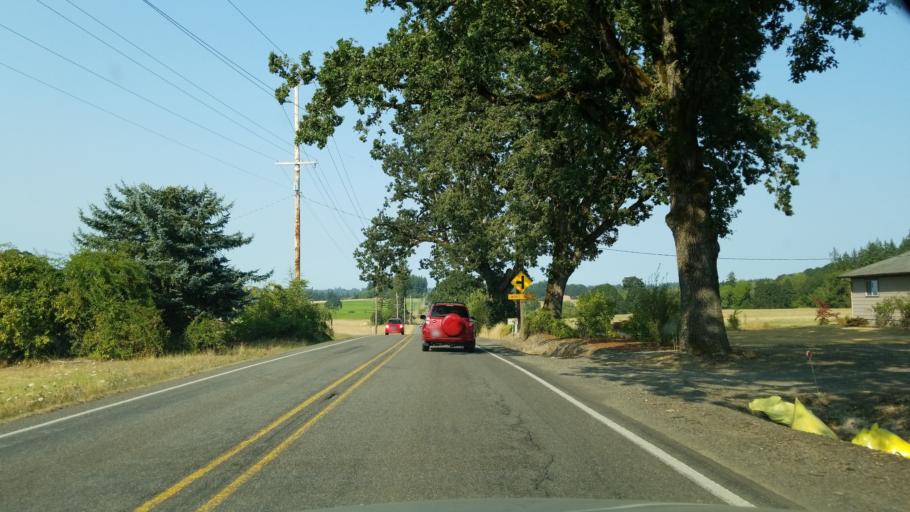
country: US
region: Oregon
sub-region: Clackamas County
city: Molalla
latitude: 45.0985
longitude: -122.6522
